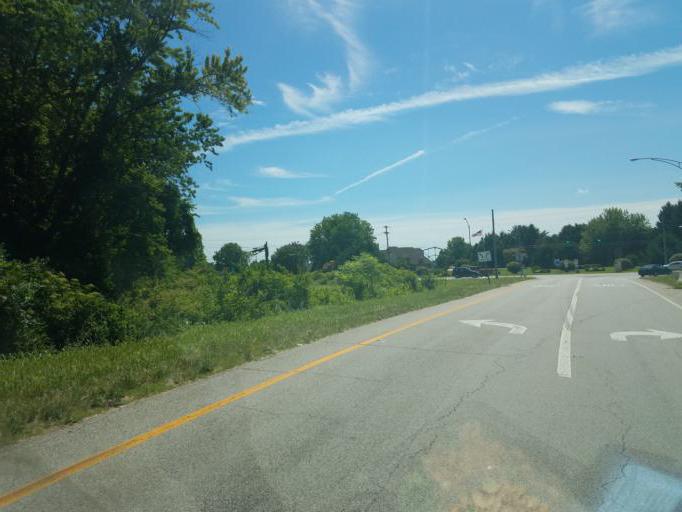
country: US
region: West Virginia
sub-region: Mason County
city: Point Pleasant
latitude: 38.8394
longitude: -82.1512
